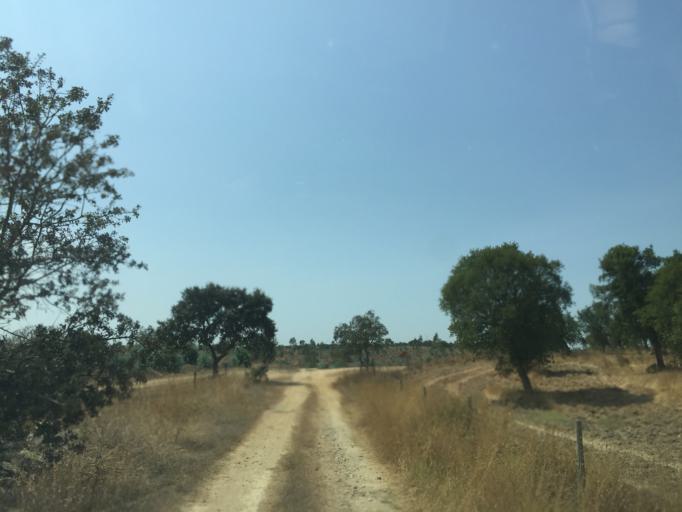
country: PT
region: Setubal
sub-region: Grandola
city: Grandola
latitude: 38.0525
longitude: -8.4551
